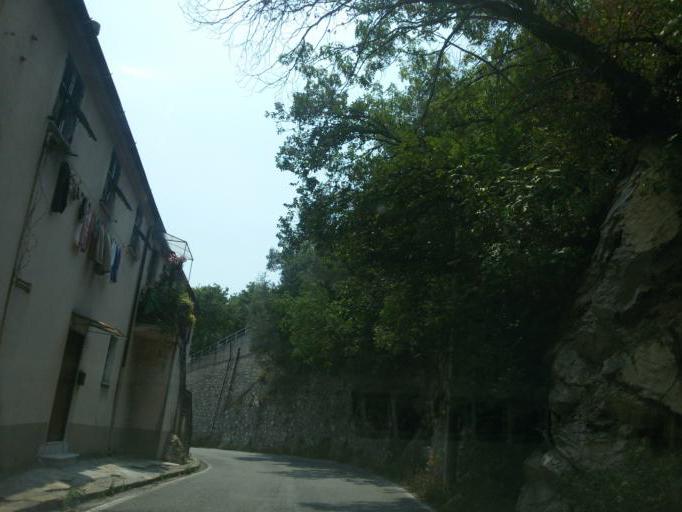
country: IT
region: Liguria
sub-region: Provincia di Genova
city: Piccarello
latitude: 44.4150
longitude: 8.9937
